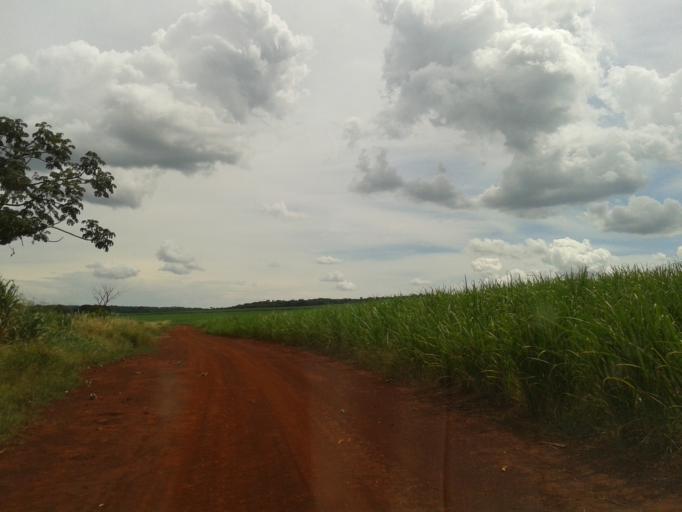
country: BR
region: Minas Gerais
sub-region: Centralina
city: Centralina
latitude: -18.6680
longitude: -49.2408
